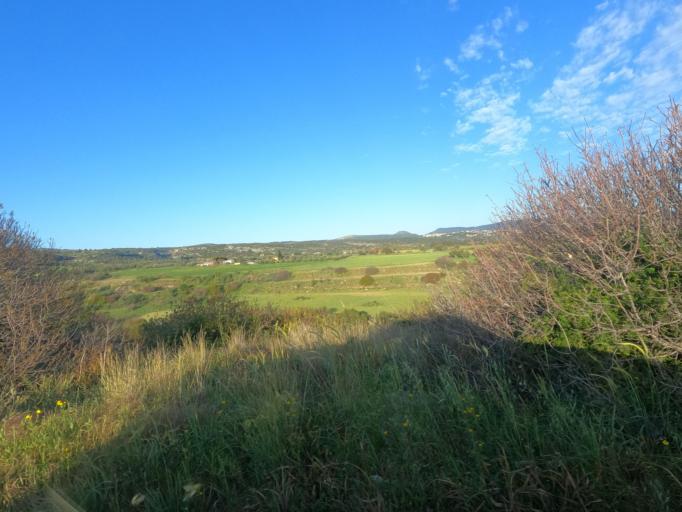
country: CY
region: Pafos
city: Polis
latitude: 35.0258
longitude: 32.3998
